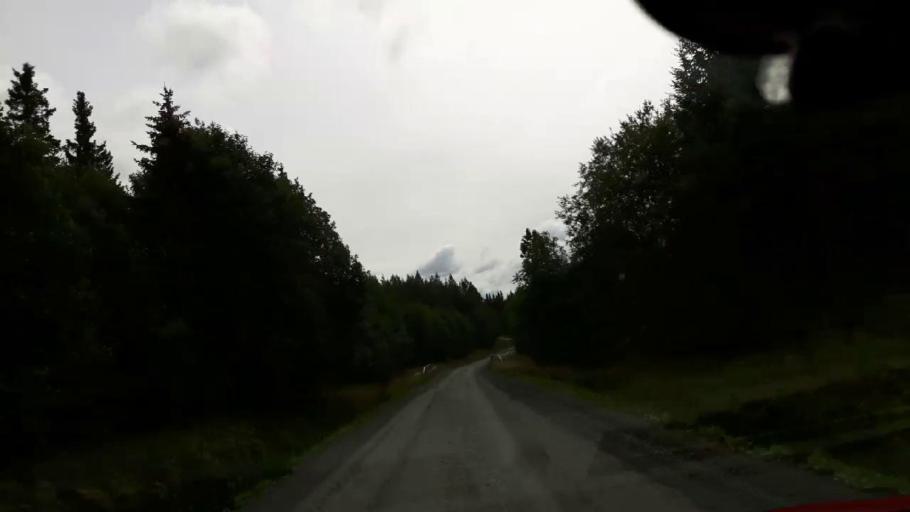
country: SE
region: Jaemtland
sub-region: Krokoms Kommun
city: Valla
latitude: 63.6642
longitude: 13.9671
